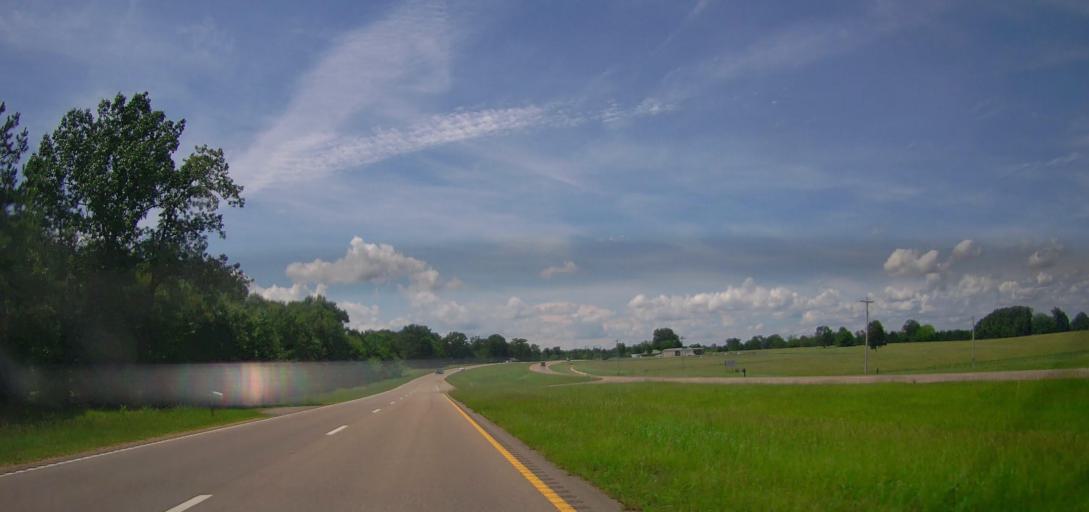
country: US
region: Mississippi
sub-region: Monroe County
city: Amory
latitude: 33.9591
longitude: -88.6106
